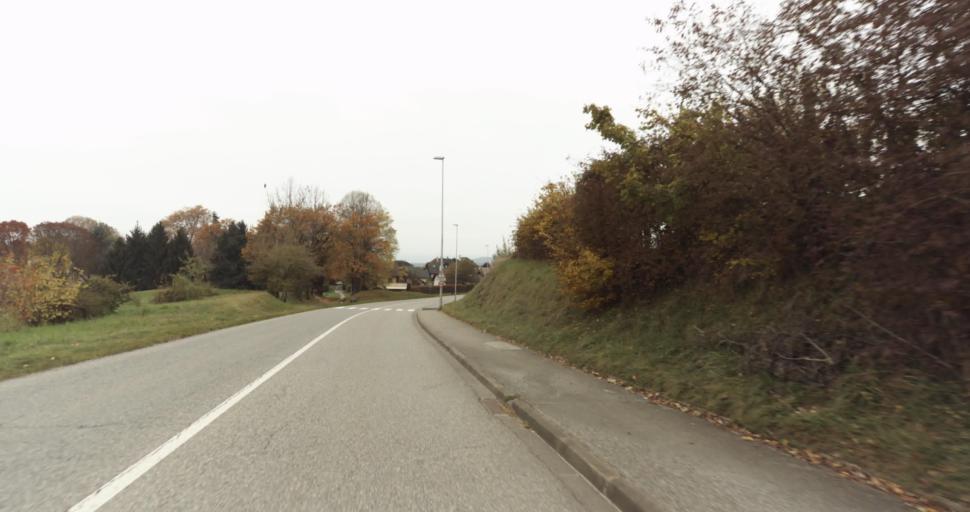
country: FR
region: Rhone-Alpes
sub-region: Departement de la Haute-Savoie
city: Annecy-le-Vieux
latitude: 45.9243
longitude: 6.1441
